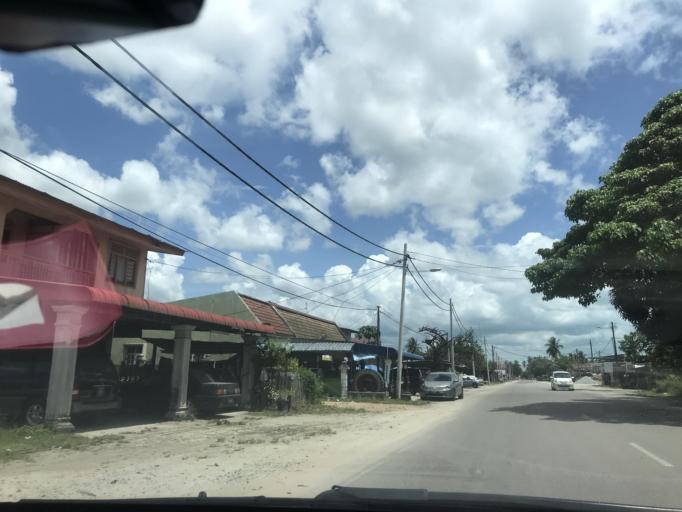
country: TH
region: Narathiwat
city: Tak Bai
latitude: 6.2274
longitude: 102.1005
